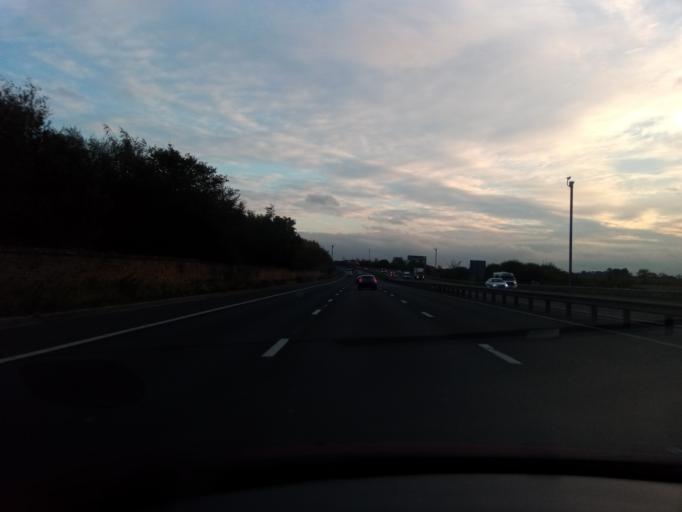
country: GB
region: England
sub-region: City and Borough of Leeds
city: Wetherby
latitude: 53.9164
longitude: -1.3853
